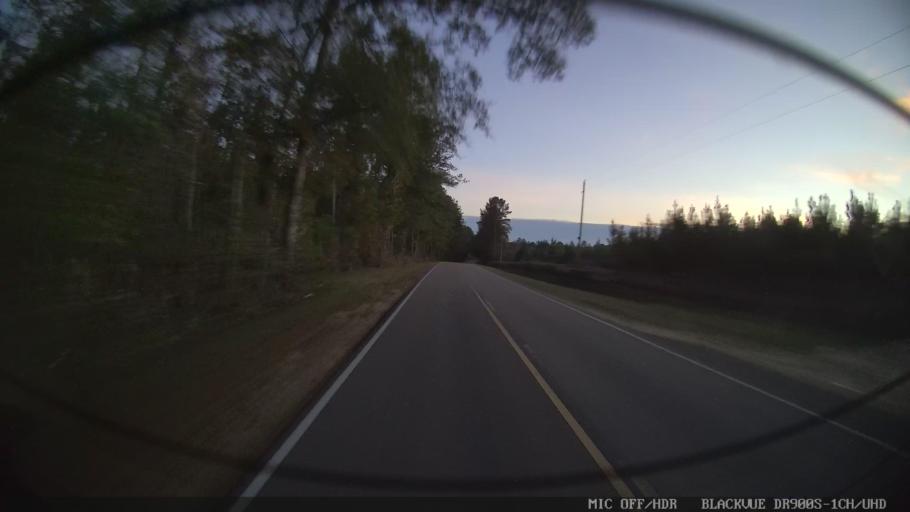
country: US
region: Mississippi
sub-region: Perry County
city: New Augusta
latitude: 31.1188
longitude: -89.1968
